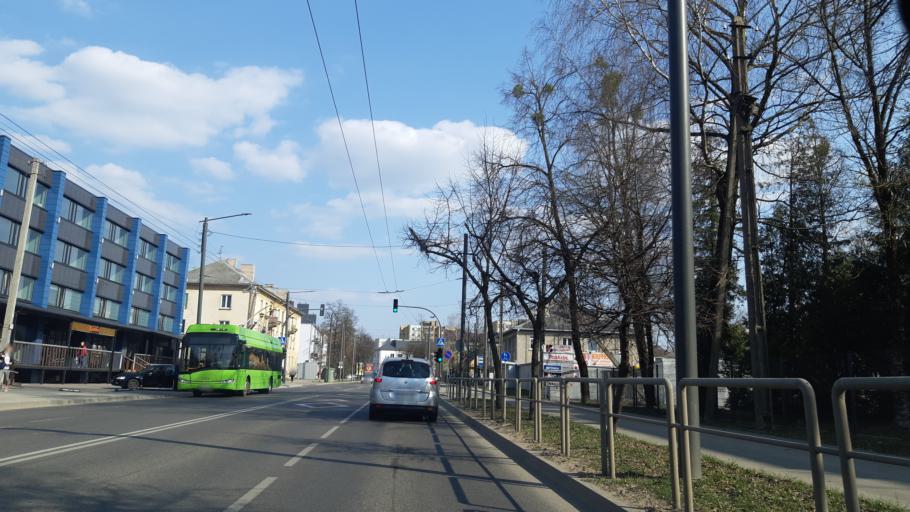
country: LT
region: Kauno apskritis
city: Dainava (Kaunas)
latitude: 54.8926
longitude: 23.9997
